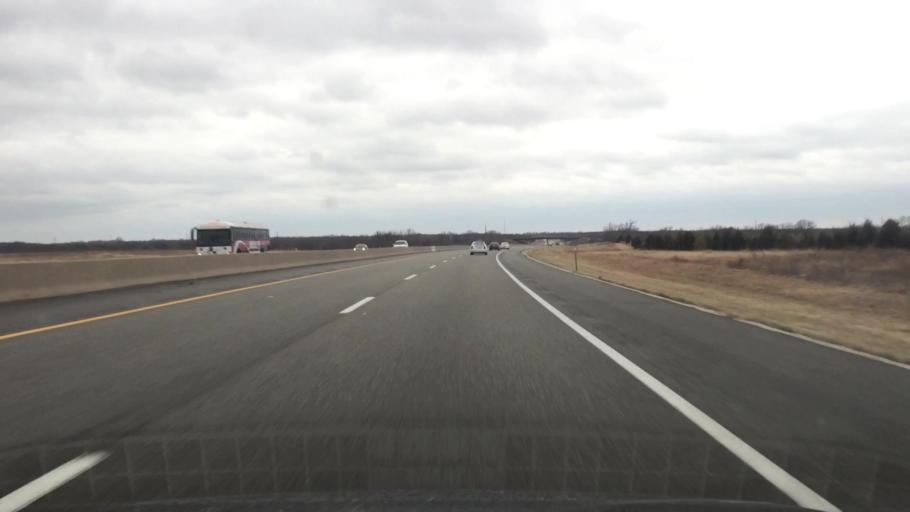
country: US
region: Kansas
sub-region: Butler County
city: Andover
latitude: 37.7369
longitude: -97.0683
